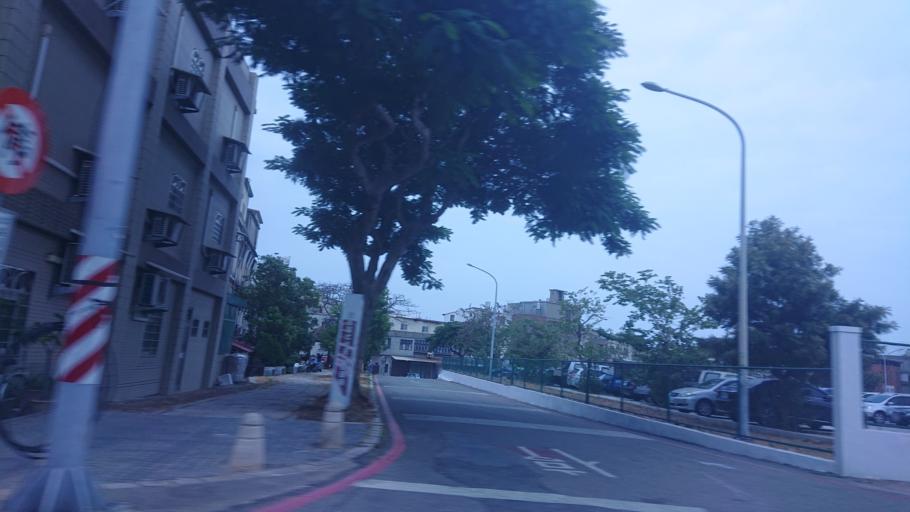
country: TW
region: Fukien
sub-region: Kinmen
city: Jincheng
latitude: 24.4343
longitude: 118.3138
